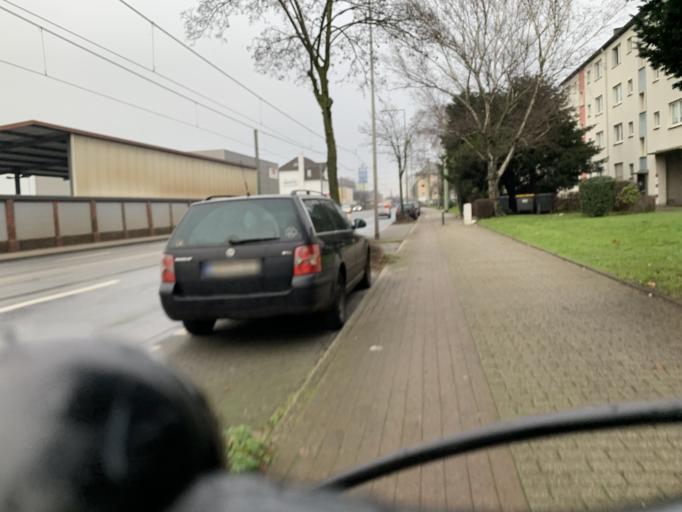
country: DE
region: North Rhine-Westphalia
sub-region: Regierungsbezirk Dusseldorf
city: Hochfeld
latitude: 51.3987
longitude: 6.7509
